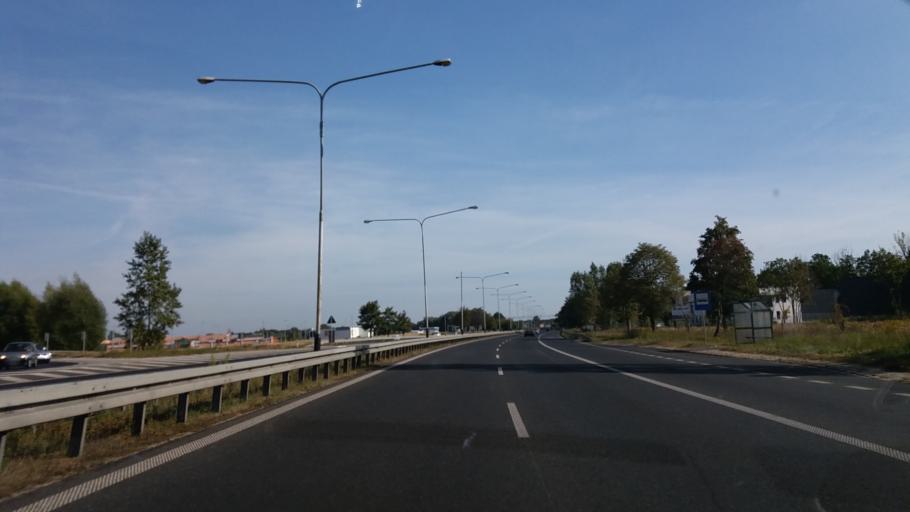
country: PL
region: Greater Poland Voivodeship
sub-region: Powiat poznanski
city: Baranowo
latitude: 52.4404
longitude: 16.7554
